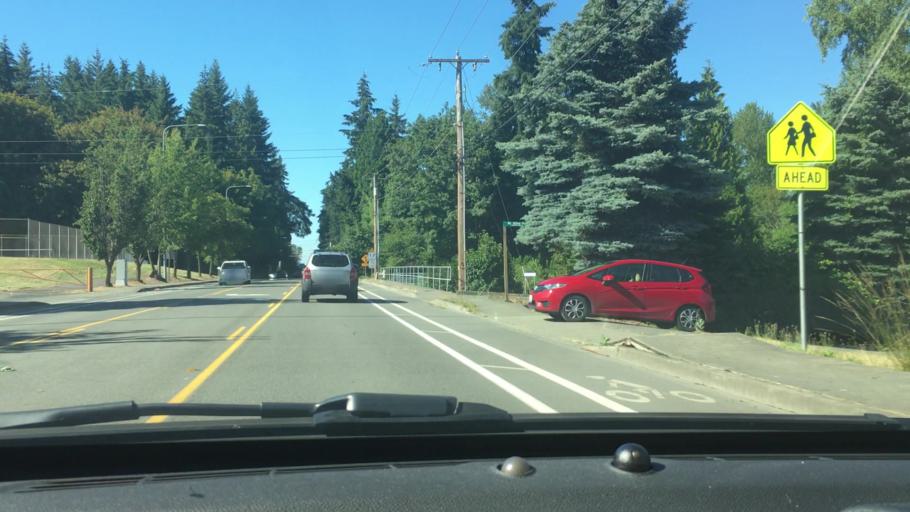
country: US
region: Washington
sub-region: King County
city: Kingsgate
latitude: 47.7281
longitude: -122.1640
